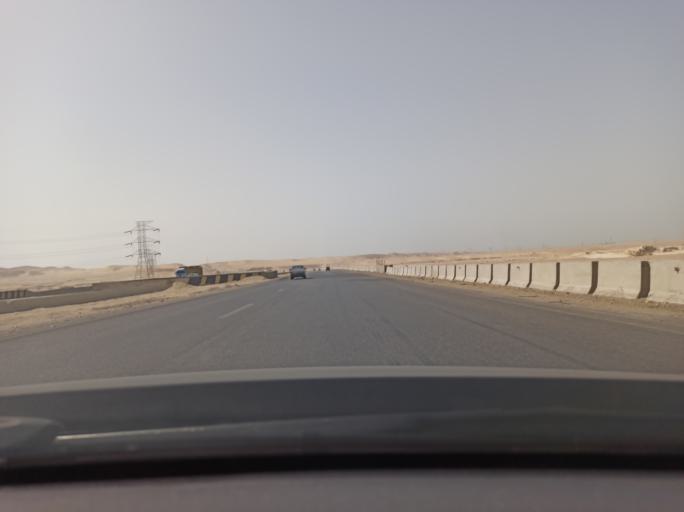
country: EG
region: Al Jizah
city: As Saff
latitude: 29.5265
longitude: 31.3849
